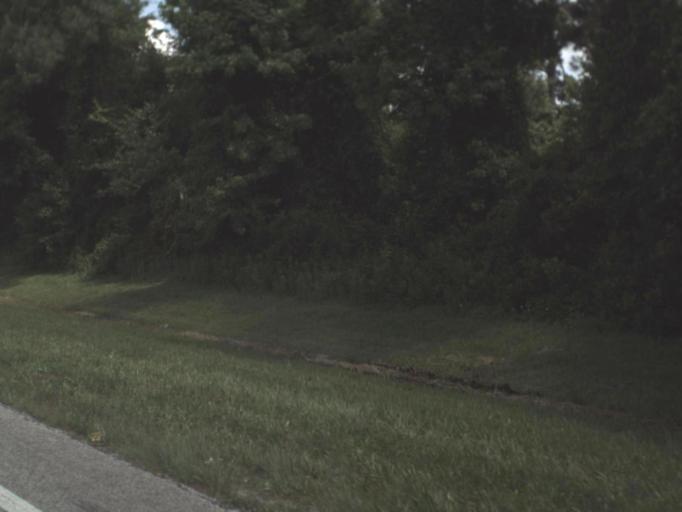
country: US
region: Florida
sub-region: Alachua County
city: Alachua
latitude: 29.7431
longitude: -82.3873
